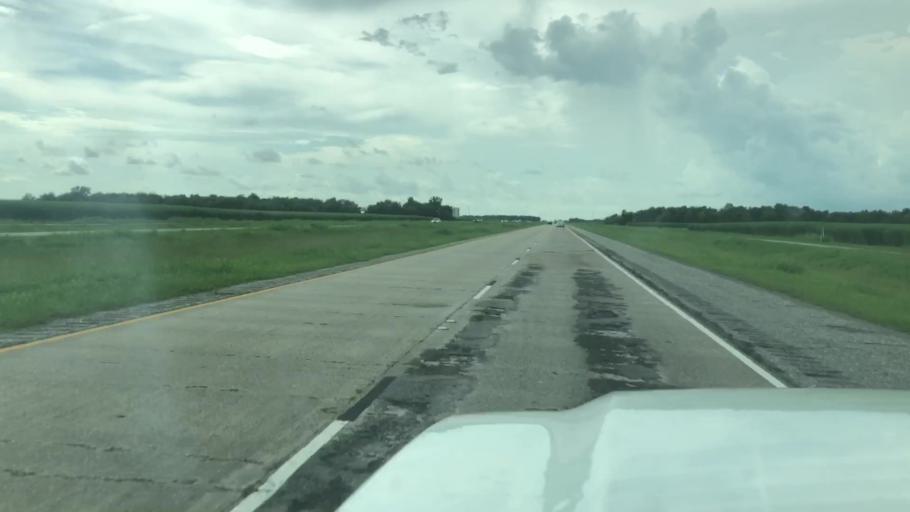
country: US
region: Louisiana
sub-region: Saint Mary Parish
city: Baldwin
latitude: 29.8458
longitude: -91.5857
